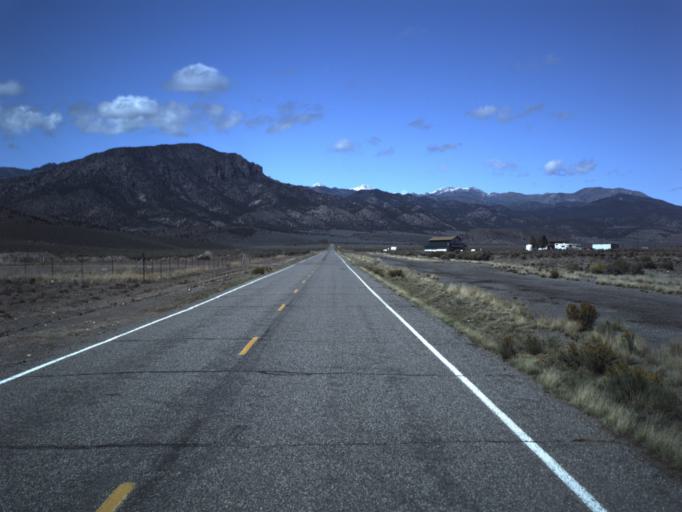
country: US
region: Utah
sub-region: Piute County
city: Junction
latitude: 38.2402
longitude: -112.2290
